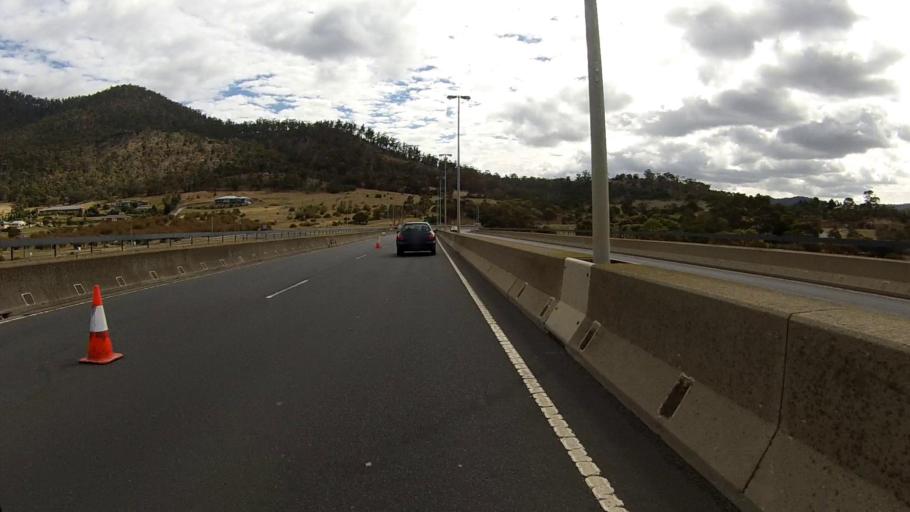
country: AU
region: Tasmania
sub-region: Glenorchy
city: Lutana
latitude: -42.8151
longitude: 147.3101
